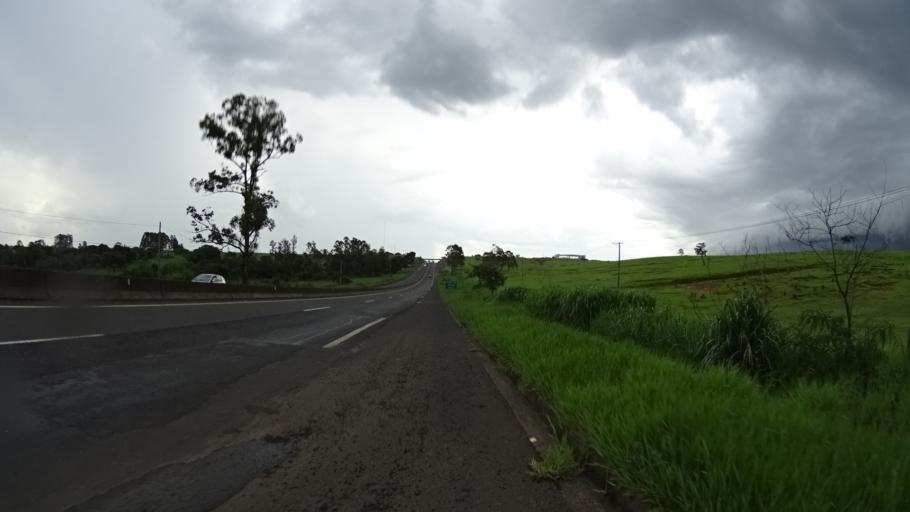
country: BR
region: Sao Paulo
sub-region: Marilia
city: Marilia
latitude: -22.2206
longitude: -49.8719
